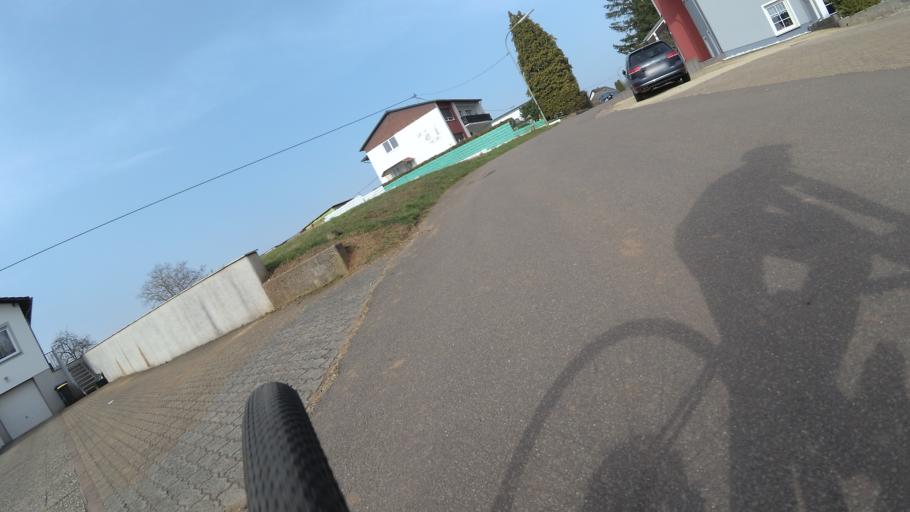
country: DE
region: Saarland
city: Nalbach
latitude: 49.4163
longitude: 6.7594
